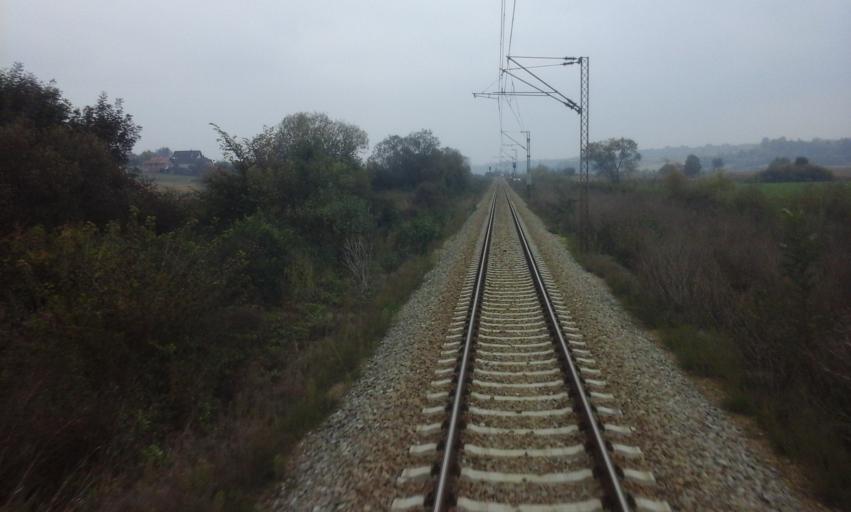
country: RS
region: Central Serbia
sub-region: Belgrade
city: Mladenovac
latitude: 44.4663
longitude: 20.6645
